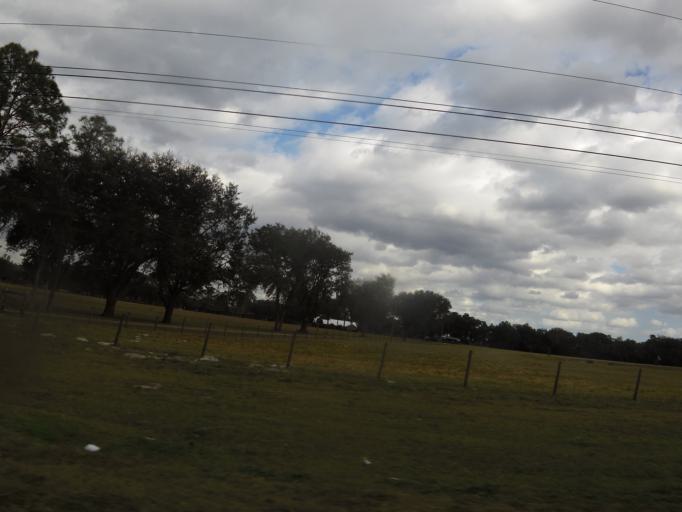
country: US
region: Florida
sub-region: Volusia County
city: Pierson
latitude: 29.3012
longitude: -81.4857
